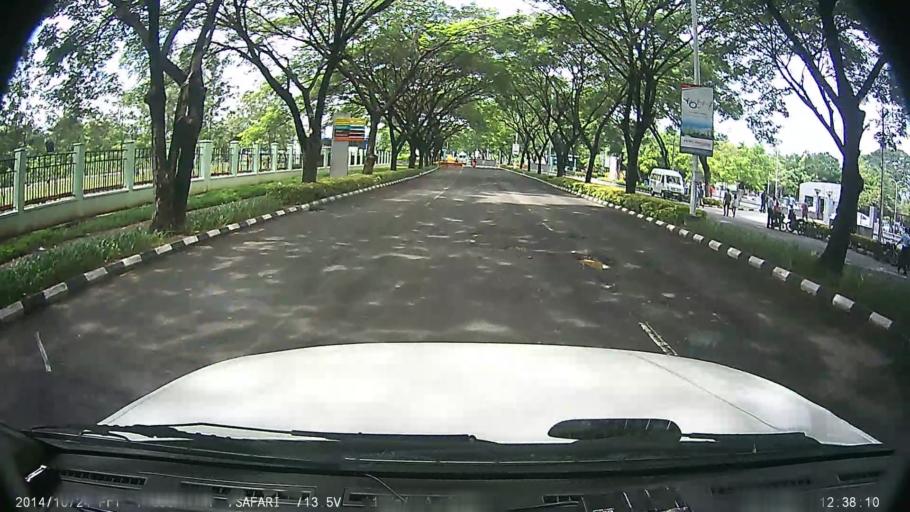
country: IN
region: Tamil Nadu
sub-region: Kancheepuram
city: Singapperumalkovil
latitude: 12.7371
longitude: 80.0046
